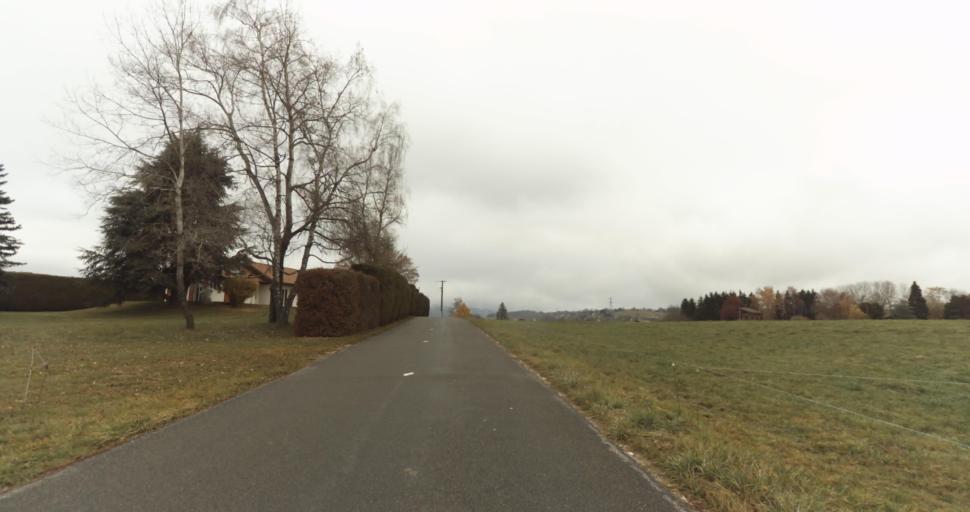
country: FR
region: Rhone-Alpes
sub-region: Departement de la Haute-Savoie
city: Groisy
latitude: 46.0357
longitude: 6.1857
